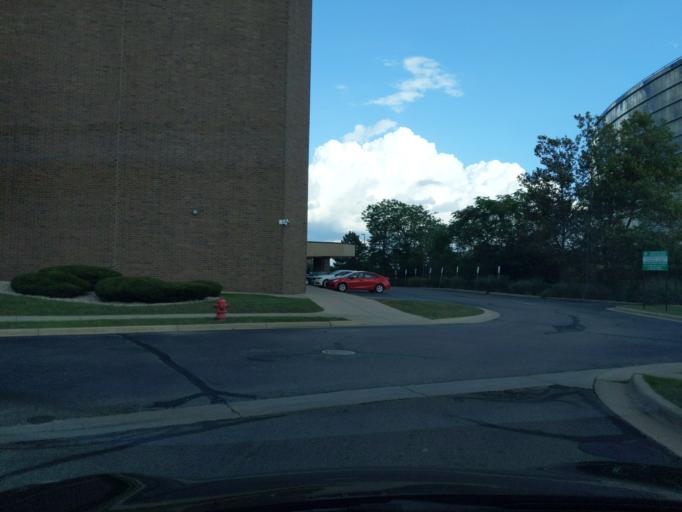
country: US
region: Michigan
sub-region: Jackson County
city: Jackson
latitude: 42.2478
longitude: -84.4032
